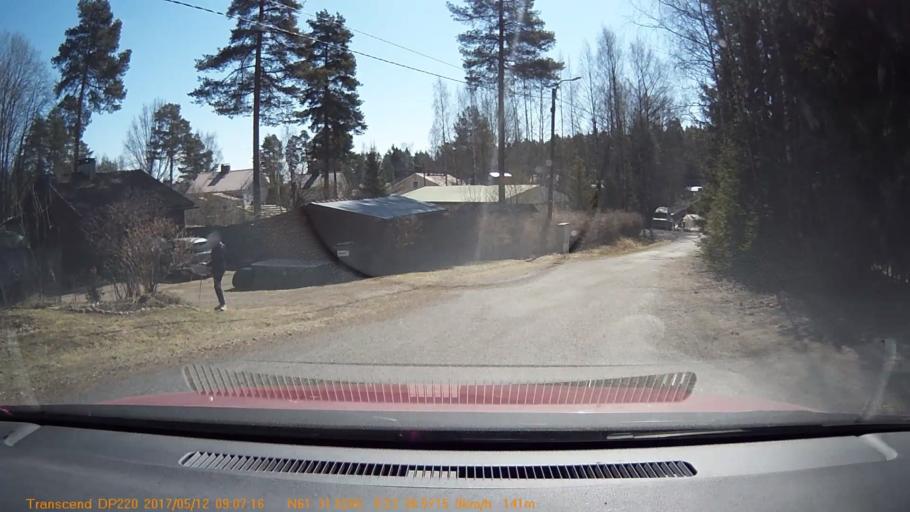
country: FI
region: Pirkanmaa
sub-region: Tampere
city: Yloejaervi
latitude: 61.5254
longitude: 23.6095
